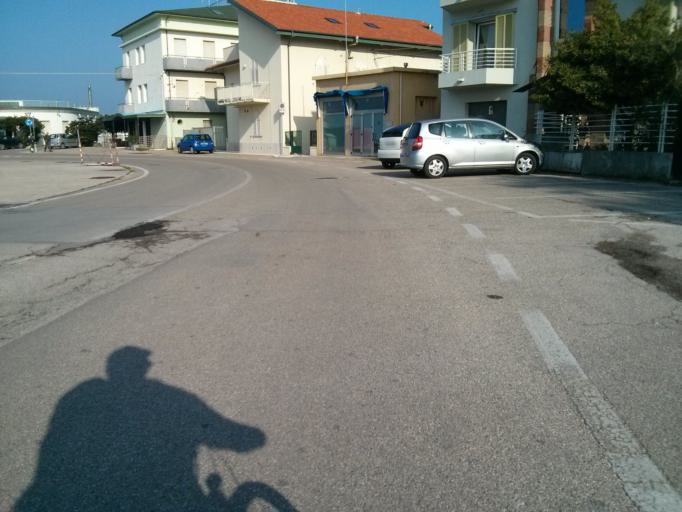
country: IT
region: The Marches
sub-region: Provincia di Pesaro e Urbino
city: Pesaro
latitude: 43.9225
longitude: 12.9065
